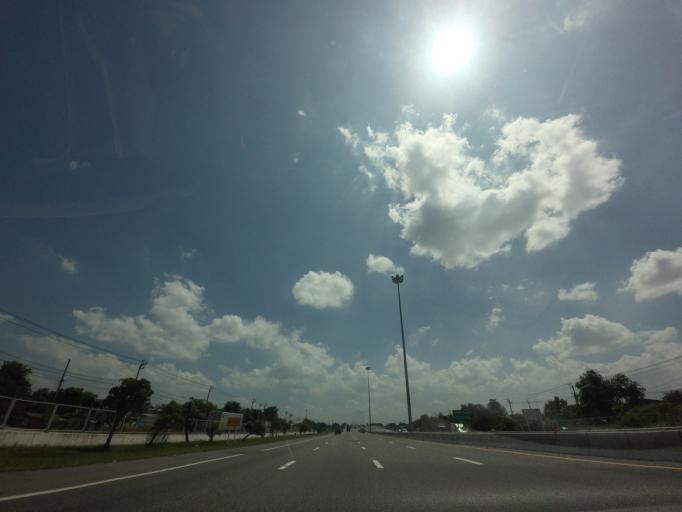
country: TH
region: Bangkok
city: Lat Krabang
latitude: 13.7180
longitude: 100.8163
